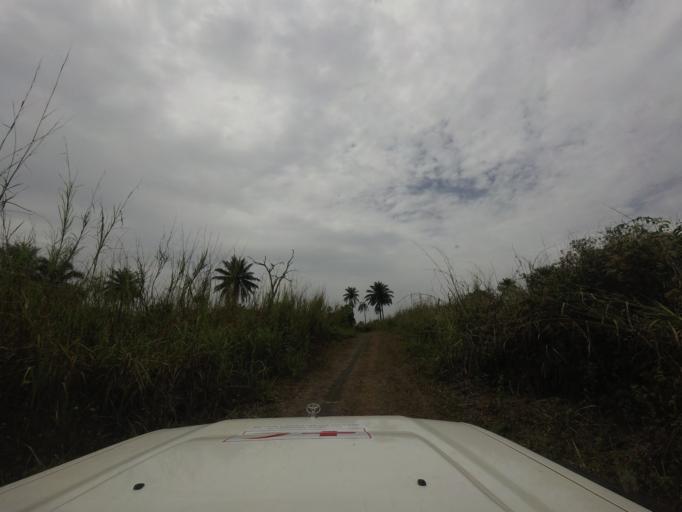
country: SL
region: Eastern Province
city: Buedu
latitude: 8.4282
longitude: -10.2650
